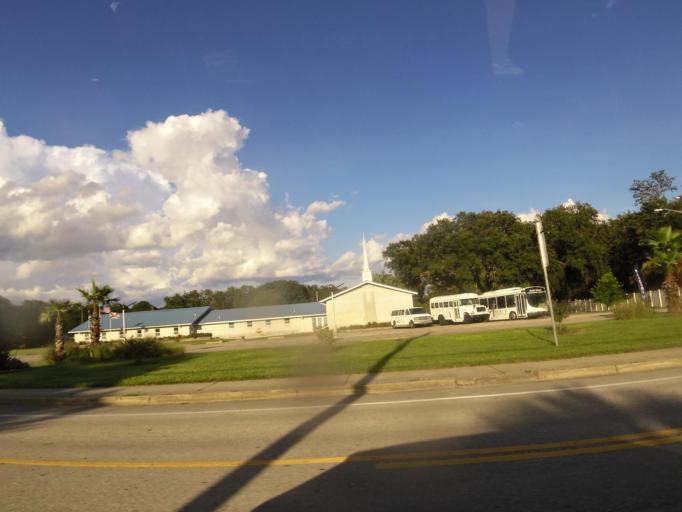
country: US
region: Florida
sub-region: Nassau County
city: Fernandina Beach
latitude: 30.6591
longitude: -81.4531
